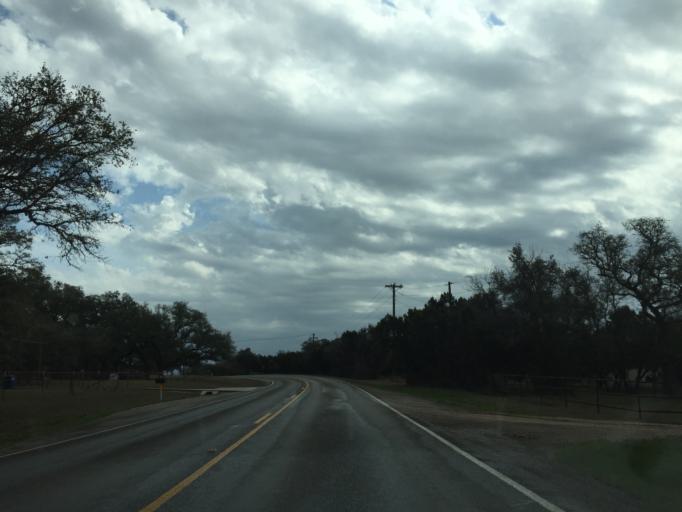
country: US
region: Texas
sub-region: Burnet County
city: Bertram
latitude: 30.6509
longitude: -97.9841
